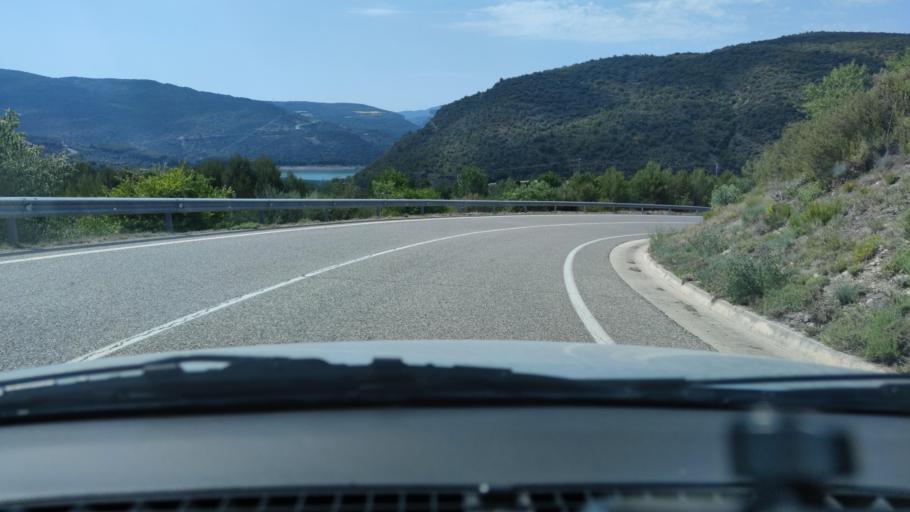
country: ES
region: Catalonia
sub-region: Provincia de Lleida
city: Ager
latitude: 42.0025
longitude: 0.8392
